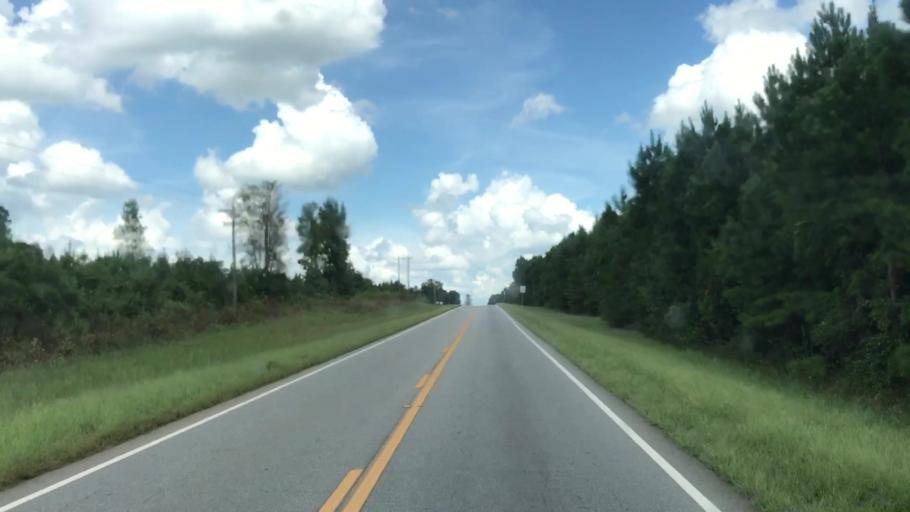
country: US
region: Georgia
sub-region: Greene County
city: Greensboro
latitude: 33.5953
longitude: -83.1959
